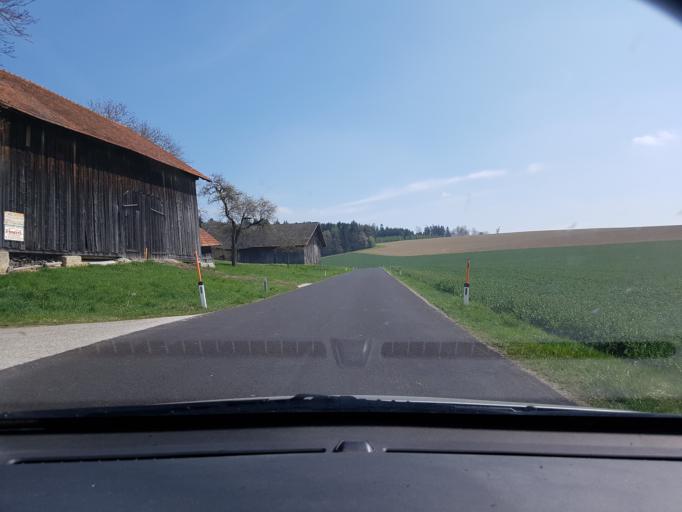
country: AT
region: Upper Austria
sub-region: Politischer Bezirk Linz-Land
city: Ansfelden
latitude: 48.2010
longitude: 14.3169
